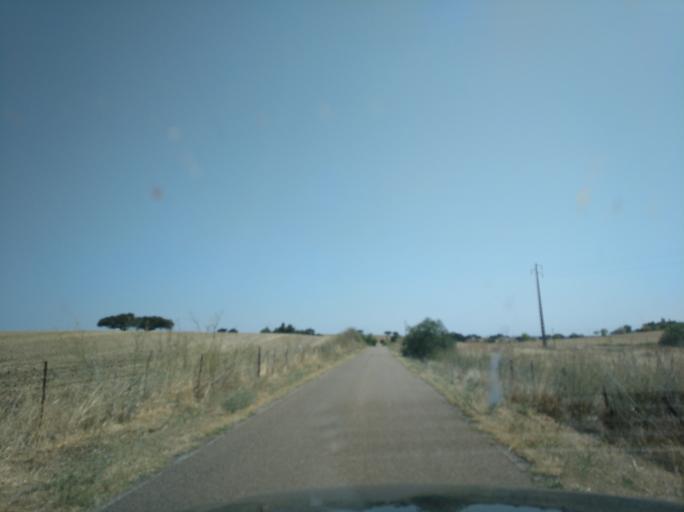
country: PT
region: Portalegre
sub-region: Campo Maior
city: Campo Maior
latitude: 39.0301
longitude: -7.0138
